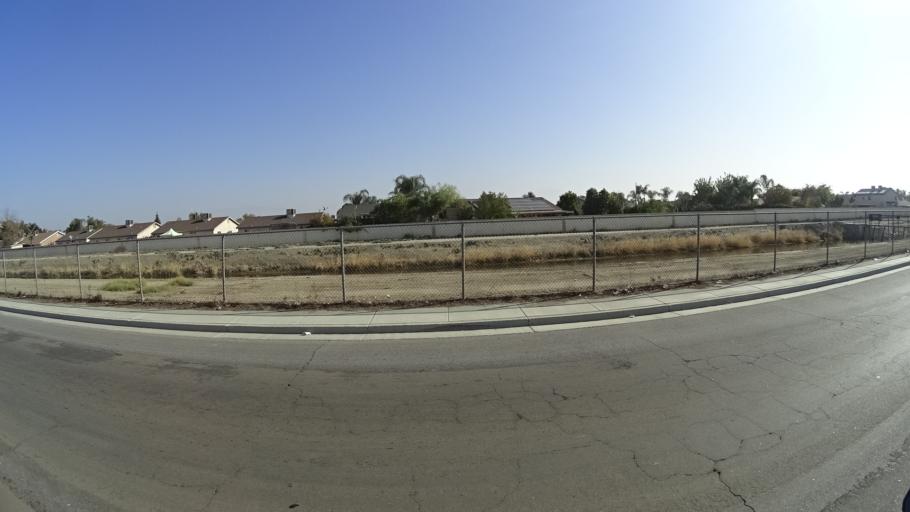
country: US
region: California
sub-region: Kern County
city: Greenfield
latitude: 35.2863
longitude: -119.0212
